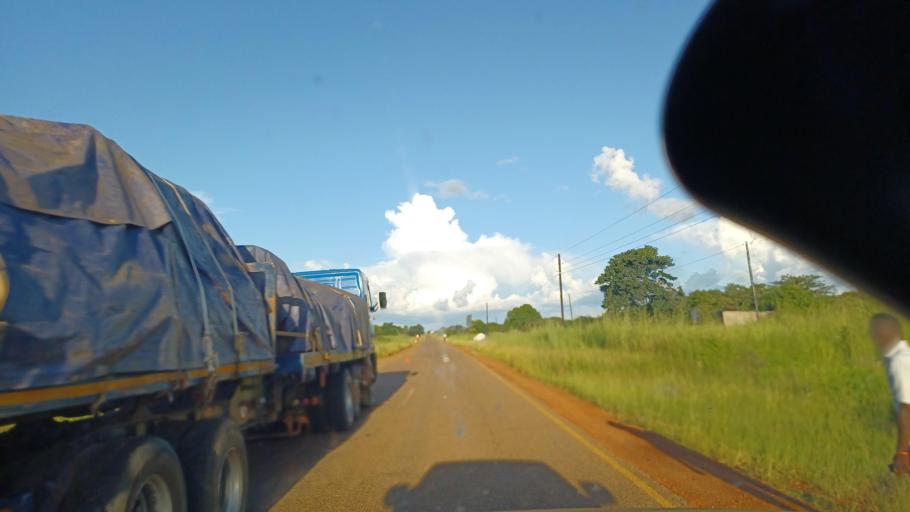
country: ZM
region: North-Western
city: Kalengwa
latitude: -13.1425
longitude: 25.0295
